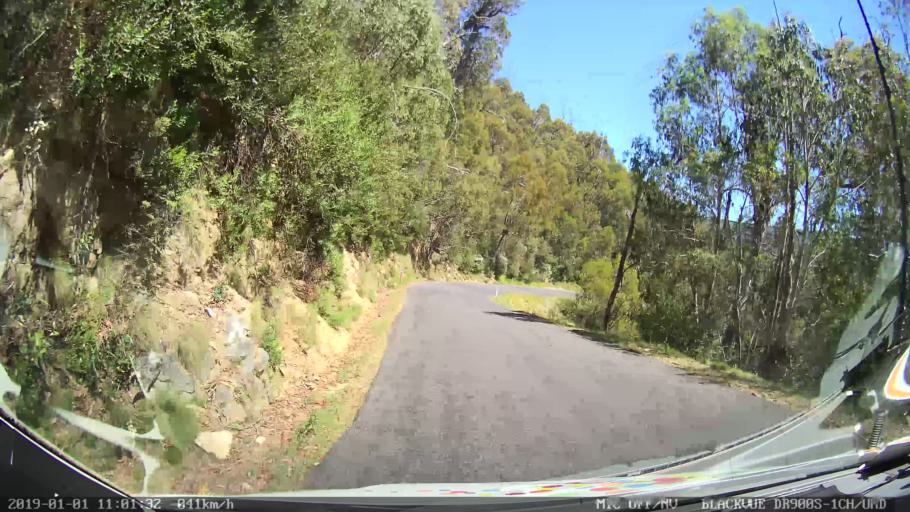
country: AU
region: New South Wales
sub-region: Snowy River
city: Jindabyne
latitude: -35.9768
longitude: 148.3987
